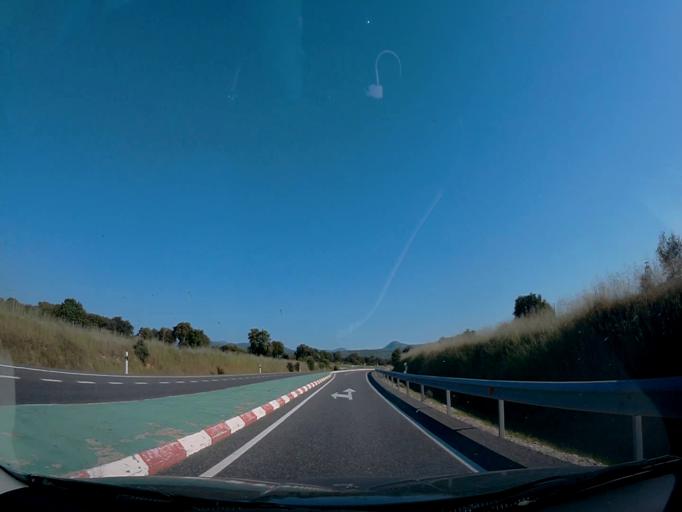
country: ES
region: Castille-La Mancha
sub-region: Province of Toledo
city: Escalona
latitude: 40.1873
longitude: -4.4038
